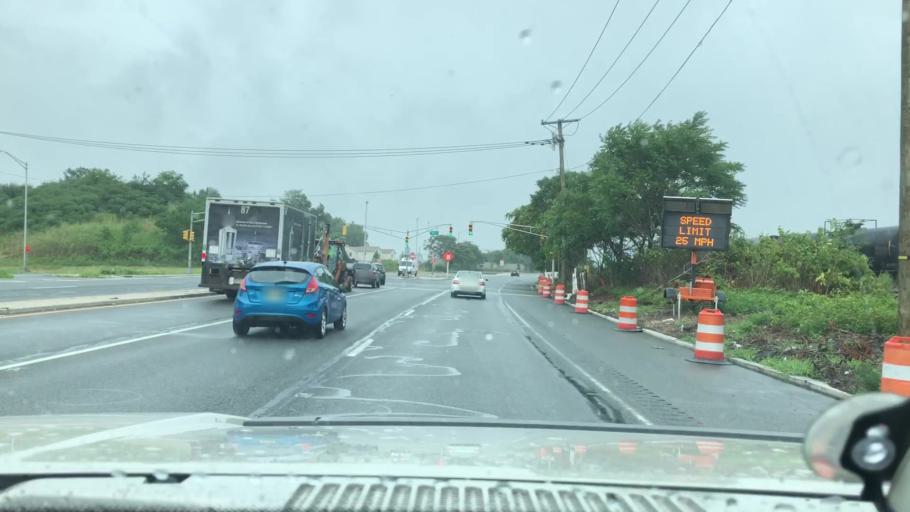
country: US
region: New Jersey
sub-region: Hudson County
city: Bayonne
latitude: 40.6568
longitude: -74.1191
